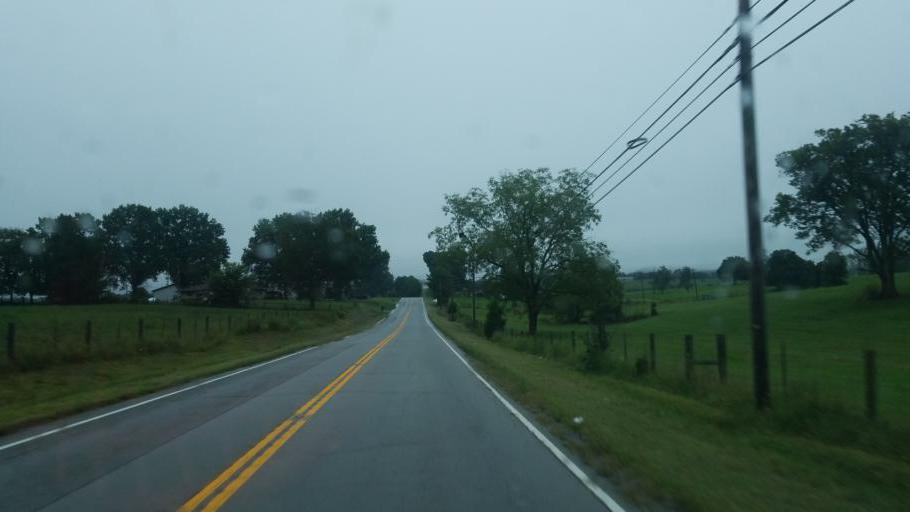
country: US
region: Kentucky
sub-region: Fleming County
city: Flemingsburg
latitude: 38.3907
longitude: -83.6802
